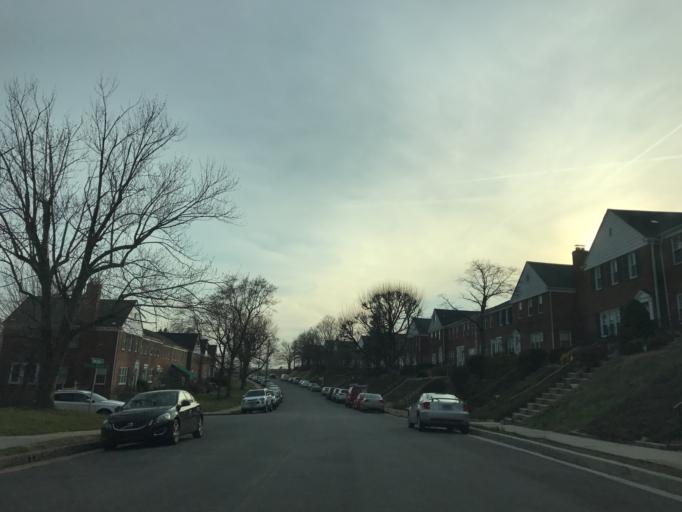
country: US
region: Maryland
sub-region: Baltimore County
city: Towson
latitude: 39.3870
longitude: -76.5731
